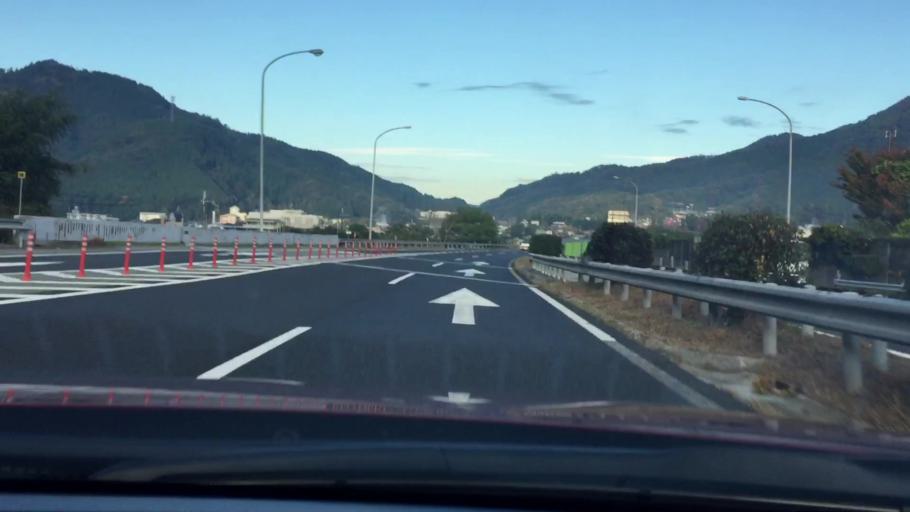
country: JP
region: Hyogo
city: Yamazakicho-nakabirose
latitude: 34.9849
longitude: 134.6016
